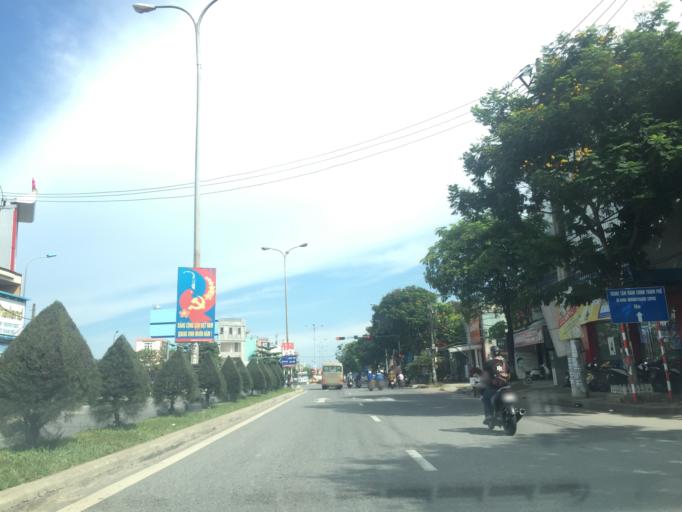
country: VN
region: Da Nang
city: Lien Chieu
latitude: 16.0659
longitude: 108.1544
